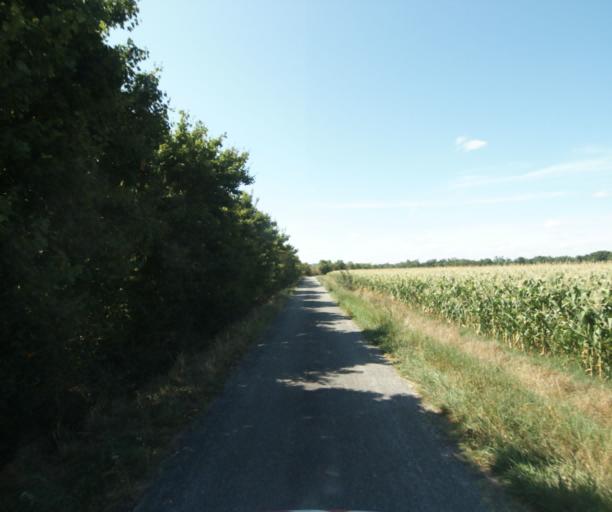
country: FR
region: Midi-Pyrenees
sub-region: Departement de la Haute-Garonne
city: Revel
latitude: 43.4849
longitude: 1.9753
